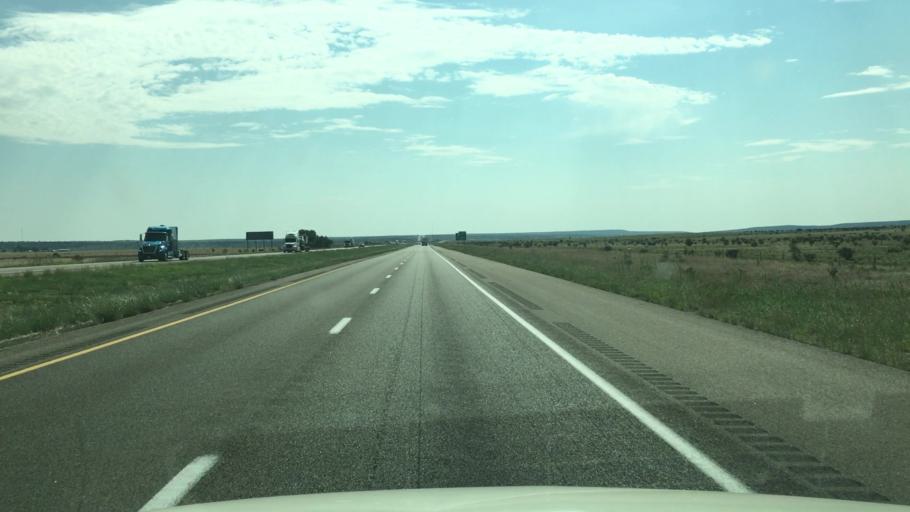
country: US
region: New Mexico
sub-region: Guadalupe County
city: Santa Rosa
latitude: 34.9776
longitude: -105.0161
